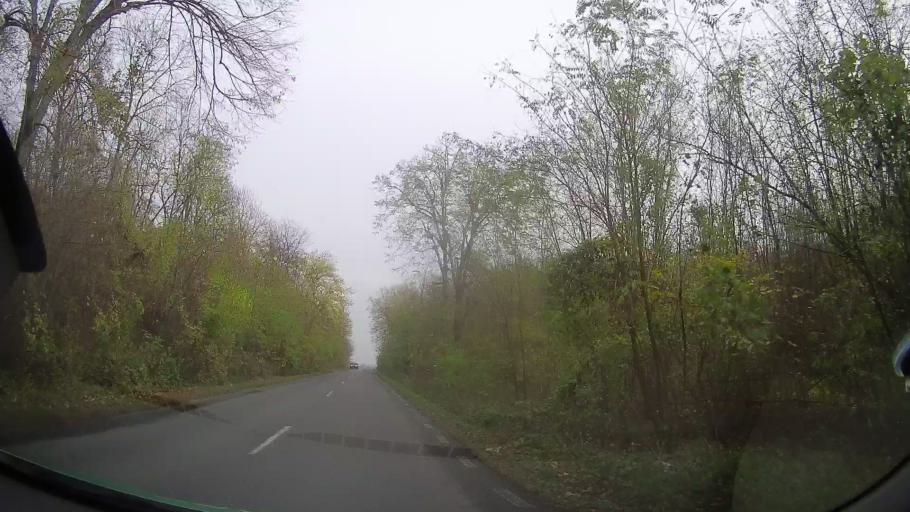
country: RO
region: Prahova
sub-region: Comuna Balta Doamnei
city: Balta Doamnei
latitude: 44.7605
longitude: 26.1330
